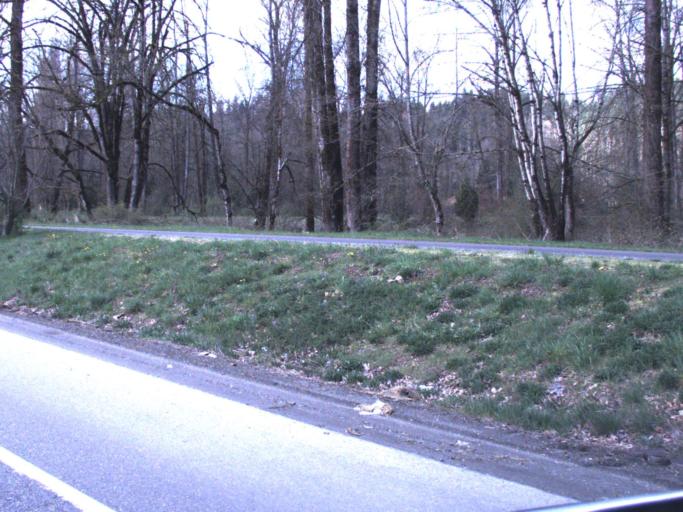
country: US
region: Washington
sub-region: King County
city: Maple Heights-Lake Desire
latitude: 47.4624
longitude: -122.0980
